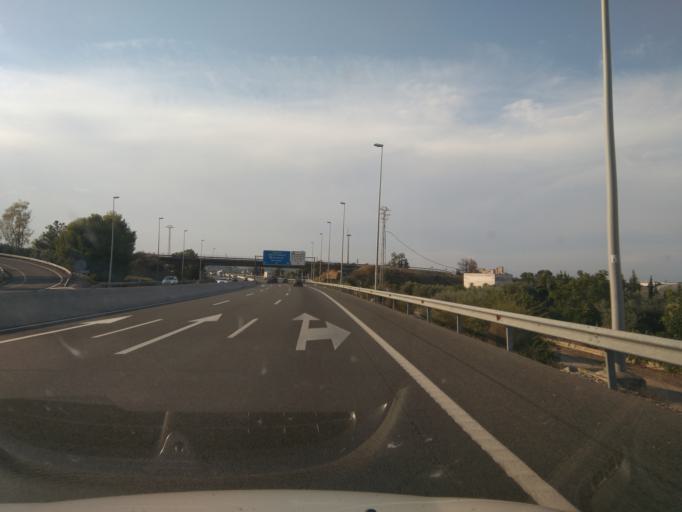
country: ES
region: Valencia
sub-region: Provincia de Valencia
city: Picassent
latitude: 39.3695
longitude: -0.4534
